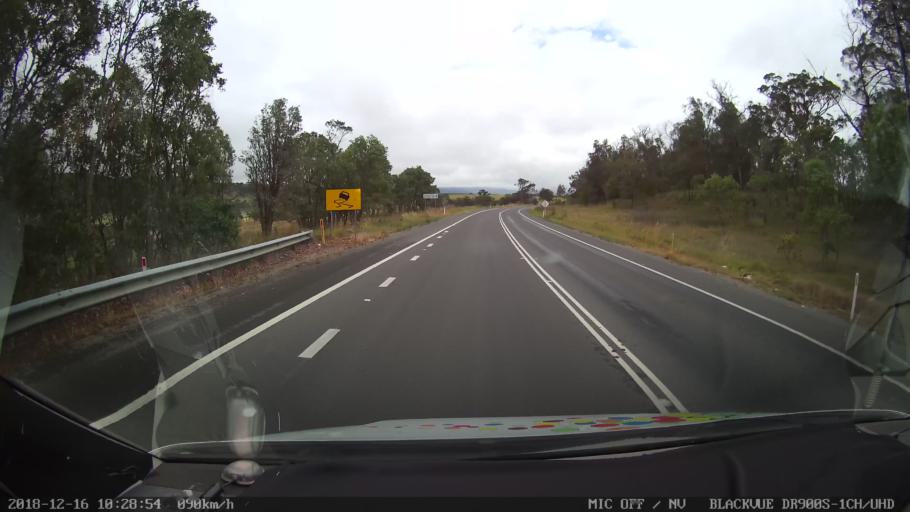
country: AU
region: New South Wales
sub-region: Tenterfield Municipality
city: Carrolls Creek
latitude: -29.1155
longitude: 151.9960
